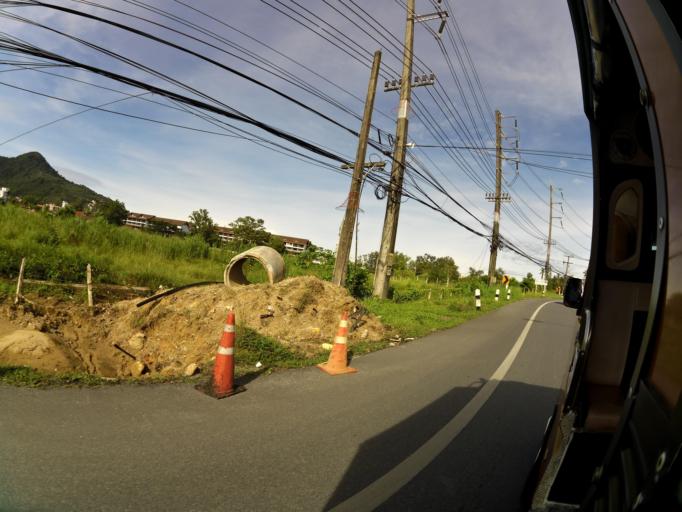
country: TH
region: Phuket
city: Patong
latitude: 7.9524
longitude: 98.2867
